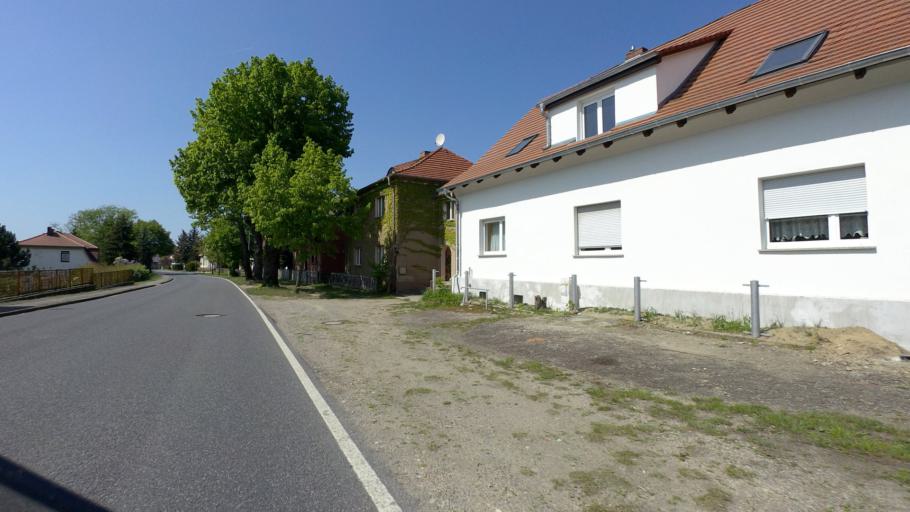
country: DE
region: Brandenburg
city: Jamlitz
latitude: 51.9912
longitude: 14.3566
